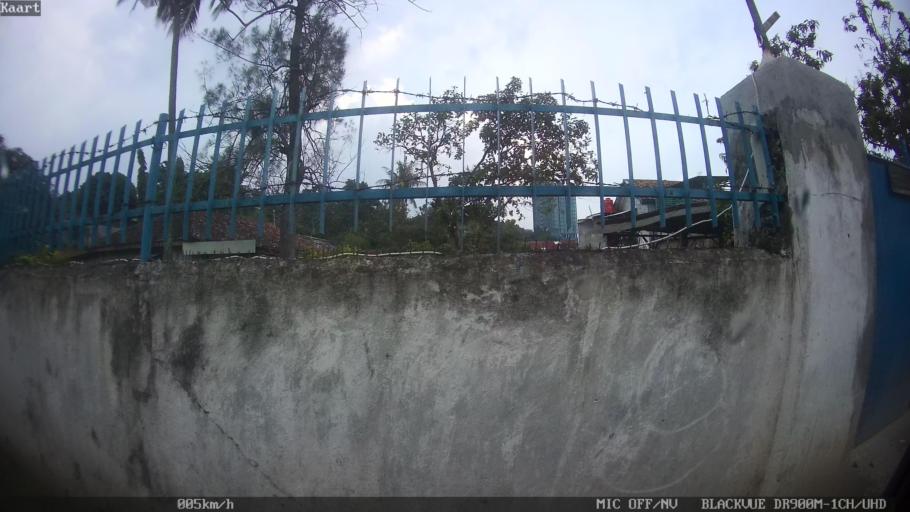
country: ID
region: Lampung
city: Bandarlampung
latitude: -5.4403
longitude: 105.2846
